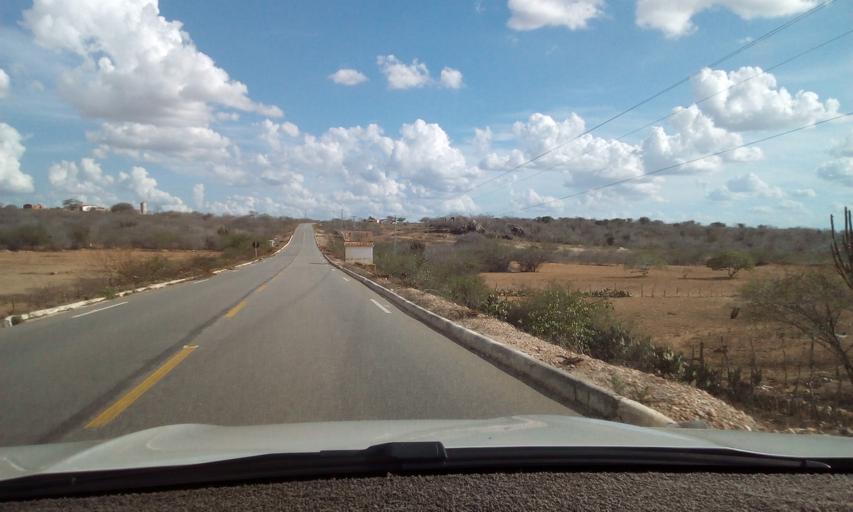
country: BR
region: Paraiba
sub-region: Soledade
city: Soledade
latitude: -6.7986
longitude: -36.4048
